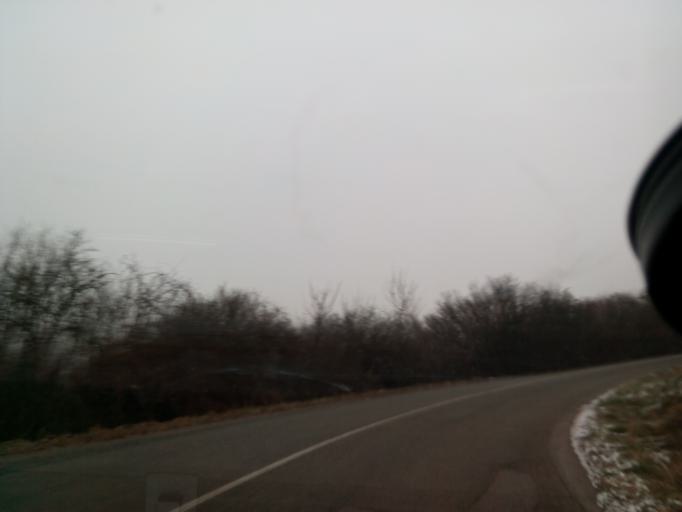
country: SK
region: Kosicky
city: Kosice
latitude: 48.7100
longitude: 21.1544
